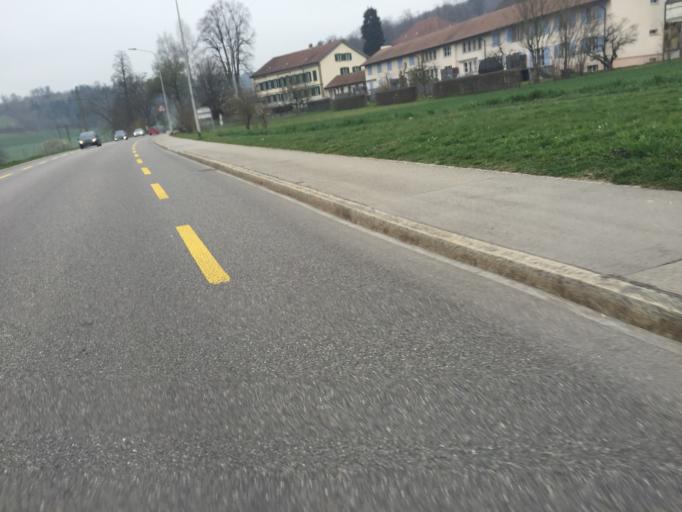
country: CH
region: Bern
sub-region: Bern-Mittelland District
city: Koniz
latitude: 46.9203
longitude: 7.4056
